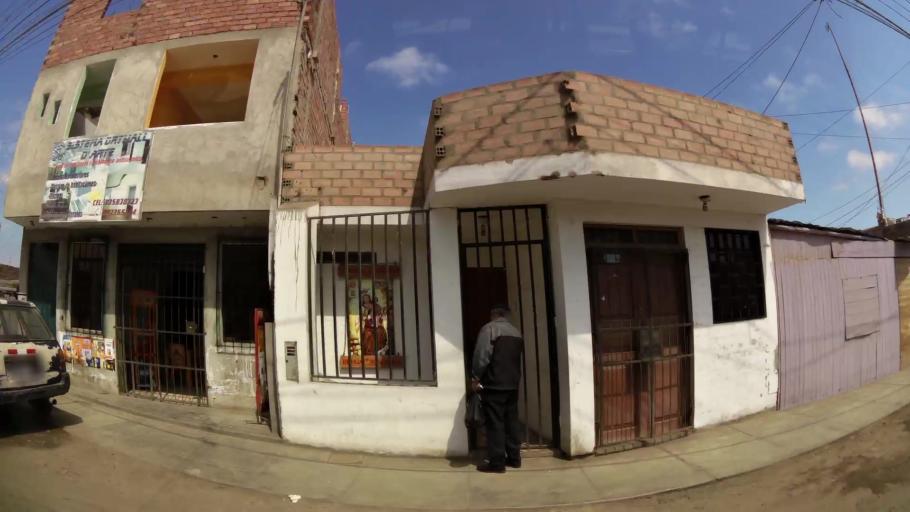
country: PE
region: Lima
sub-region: Provincia de Canete
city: Mala
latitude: -12.6548
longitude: -76.6322
